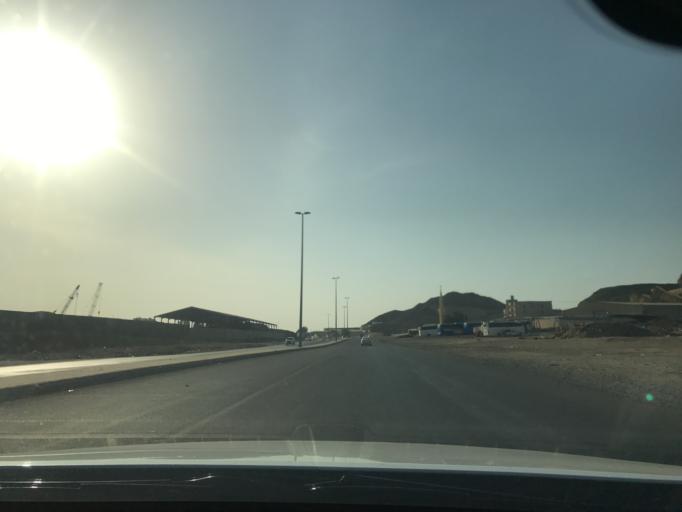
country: SA
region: Makkah
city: Jeddah
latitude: 21.4094
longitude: 39.4250
